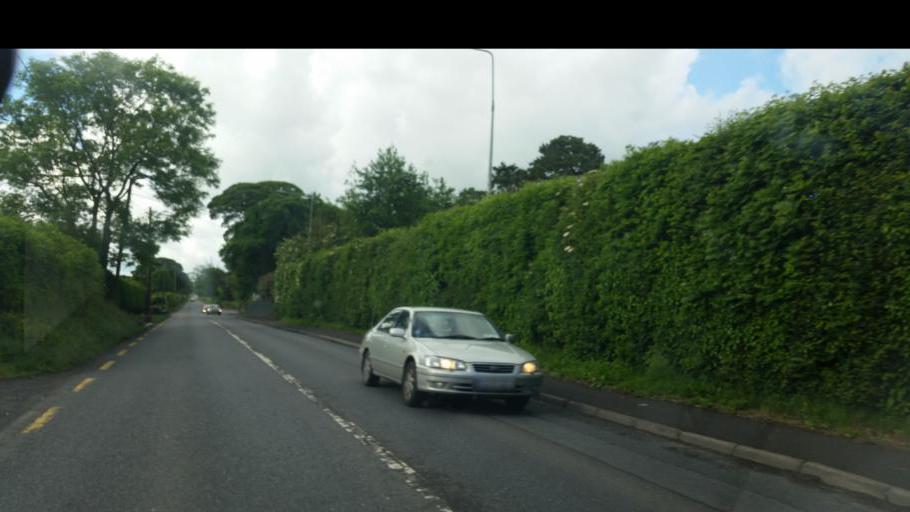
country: IE
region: Leinster
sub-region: Kildare
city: Maynooth
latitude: 53.3610
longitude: -6.5922
